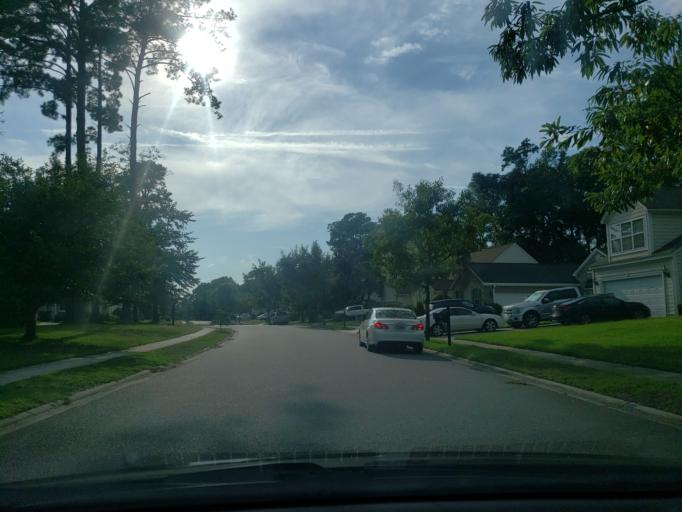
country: US
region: Georgia
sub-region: Chatham County
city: Montgomery
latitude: 31.9557
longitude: -81.1487
